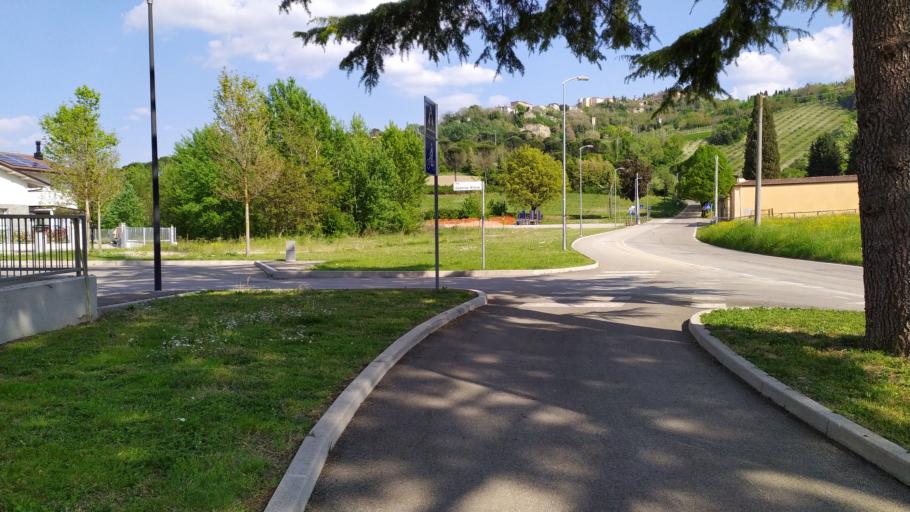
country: IT
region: Emilia-Romagna
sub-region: Provincia di Bologna
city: Borgo Tossignano
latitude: 44.2762
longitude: 11.5940
